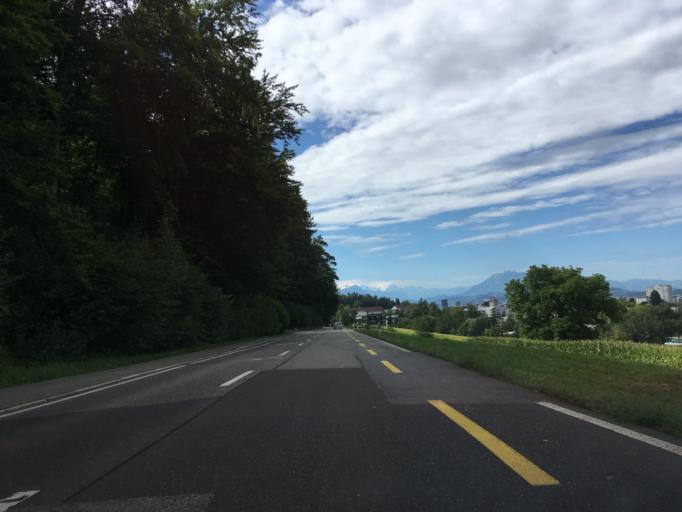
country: CH
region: Zug
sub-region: Zug
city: Baar
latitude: 47.2040
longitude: 8.5443
